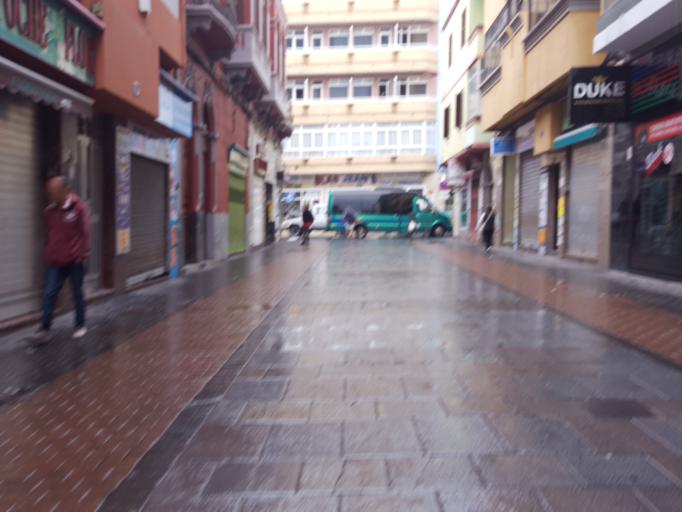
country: ES
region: Canary Islands
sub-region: Provincia de Las Palmas
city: Las Palmas de Gran Canaria
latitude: 28.1404
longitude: -15.4333
